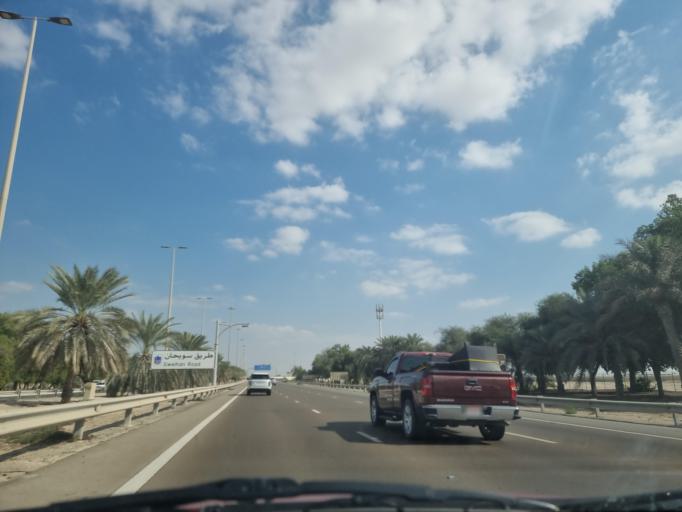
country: AE
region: Abu Dhabi
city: Abu Dhabi
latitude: 24.4095
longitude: 54.6598
